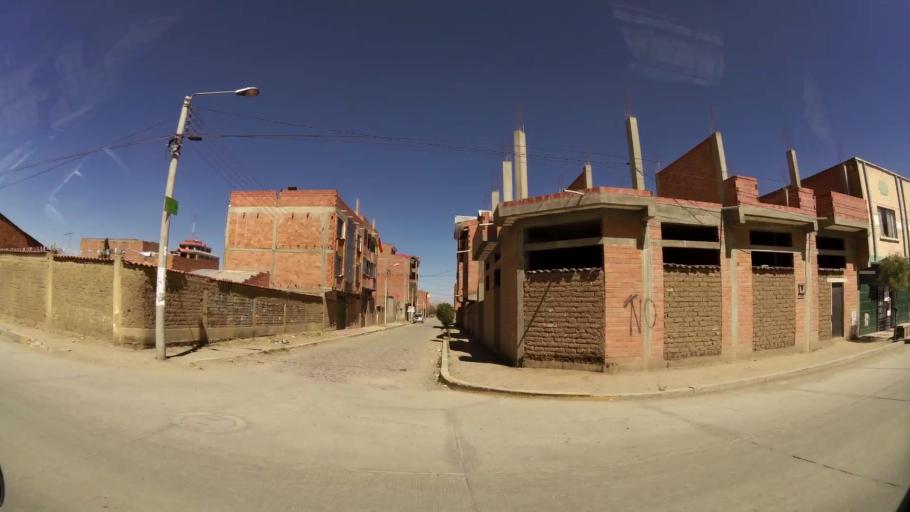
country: BO
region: La Paz
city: La Paz
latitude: -16.5045
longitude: -68.2210
